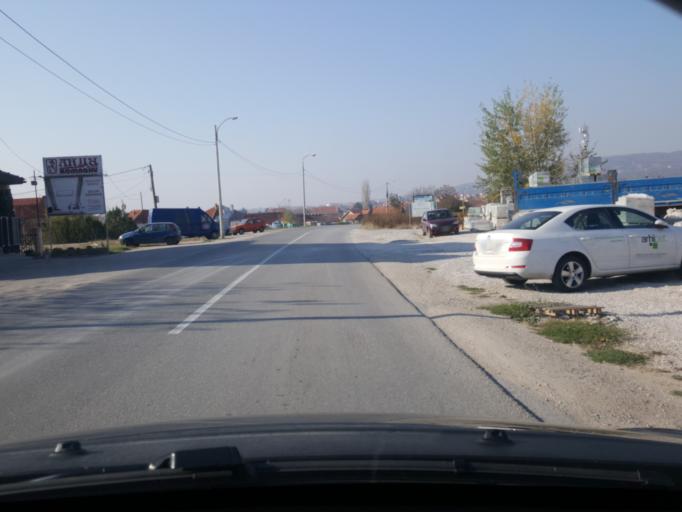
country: RS
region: Central Serbia
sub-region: Nisavski Okrug
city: Nis
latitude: 43.3291
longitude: 21.9543
